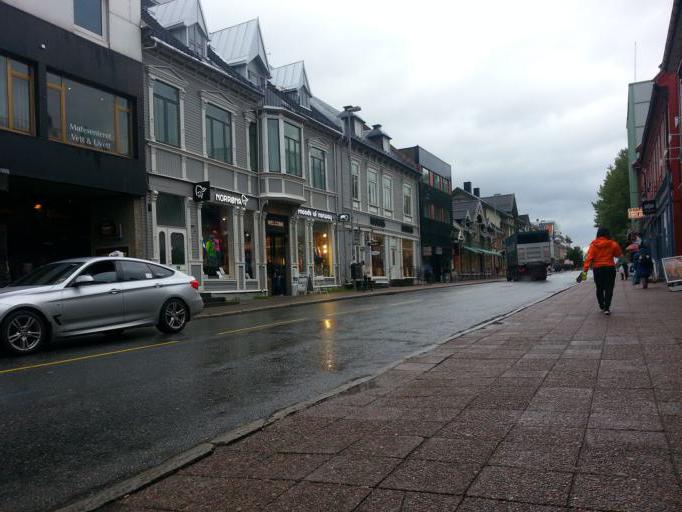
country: NO
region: Troms
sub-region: Tromso
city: Tromso
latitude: 69.6480
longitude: 18.9543
